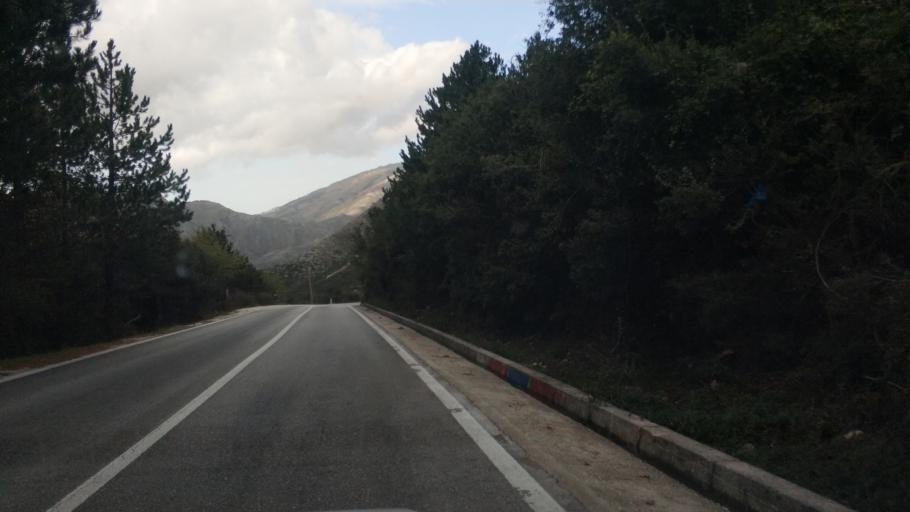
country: AL
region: Vlore
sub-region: Rrethi i Vlores
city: Brataj
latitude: 40.2273
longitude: 19.5781
